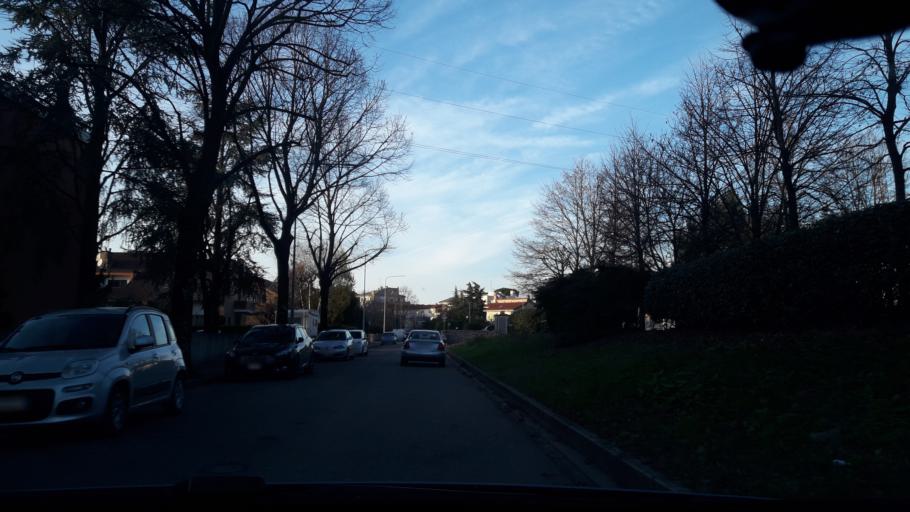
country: IT
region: Friuli Venezia Giulia
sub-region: Provincia di Udine
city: Udine
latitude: 46.0505
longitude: 13.2556
